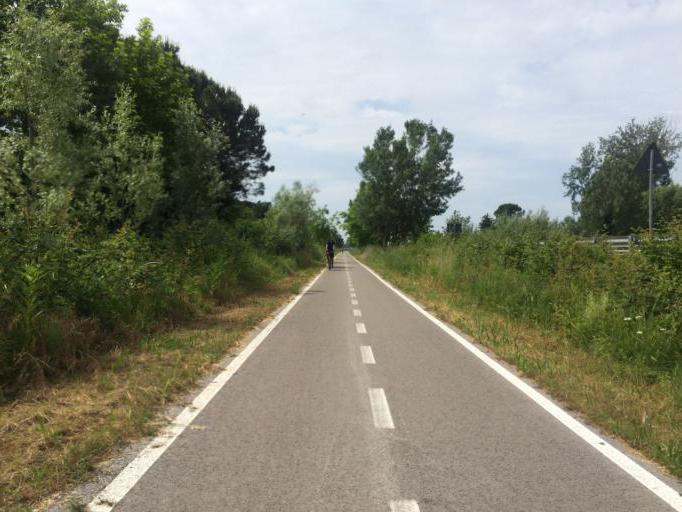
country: IT
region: Friuli Venezia Giulia
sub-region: Provincia di Udine
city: Aquileia
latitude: 45.7281
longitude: 13.3878
